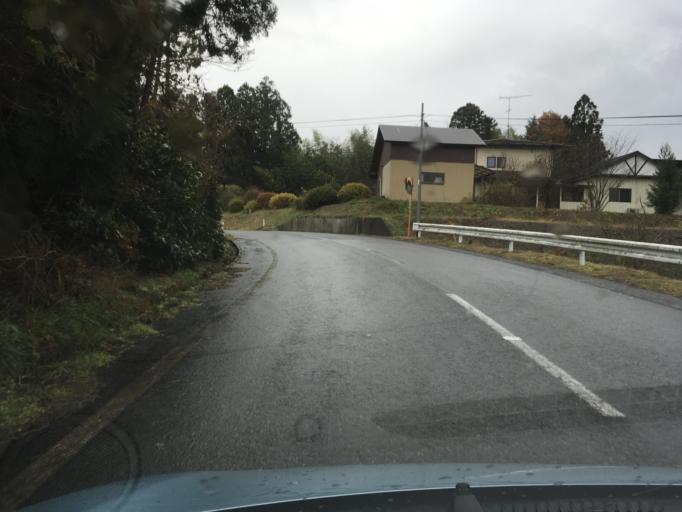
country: JP
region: Iwate
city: Ichinoseki
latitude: 38.7884
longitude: 141.2321
